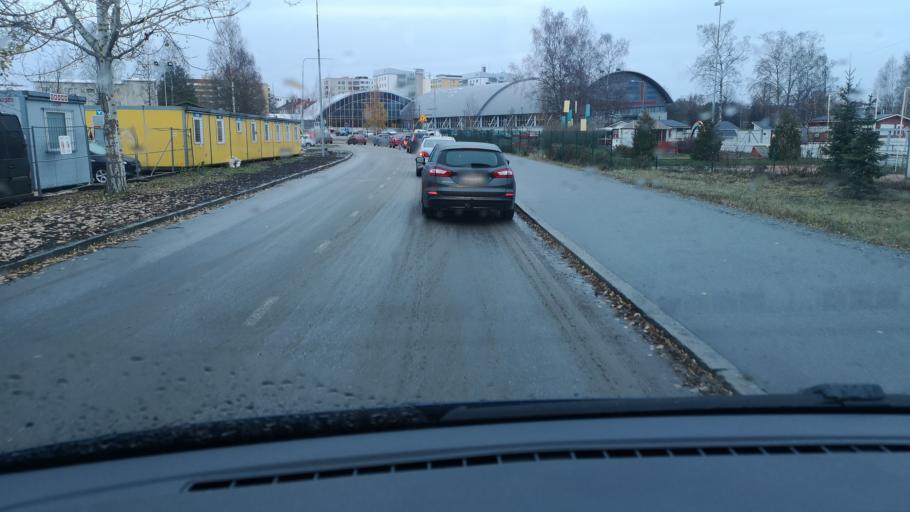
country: FI
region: Ostrobothnia
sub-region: Vaasa
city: Vaasa
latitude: 63.0846
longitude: 21.6201
